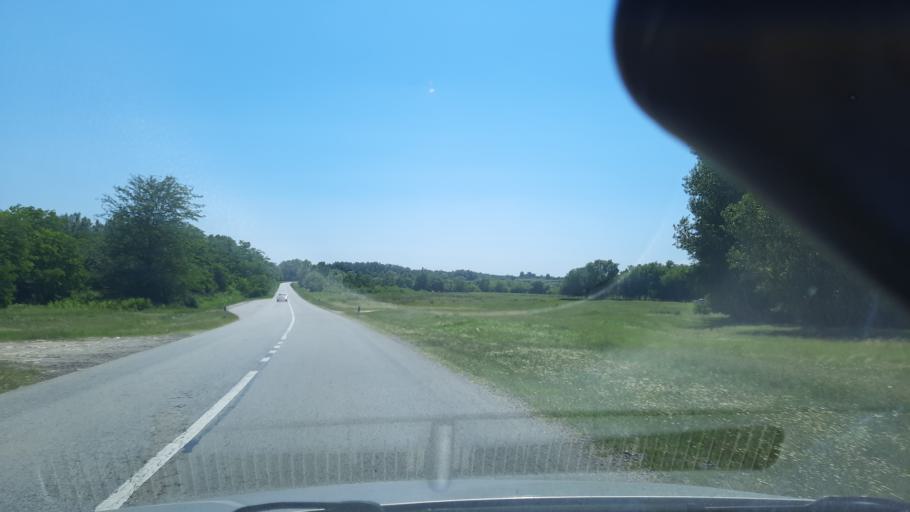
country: RO
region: Caras-Severin
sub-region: Comuna Socol
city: Socol
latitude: 44.8631
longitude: 21.3077
